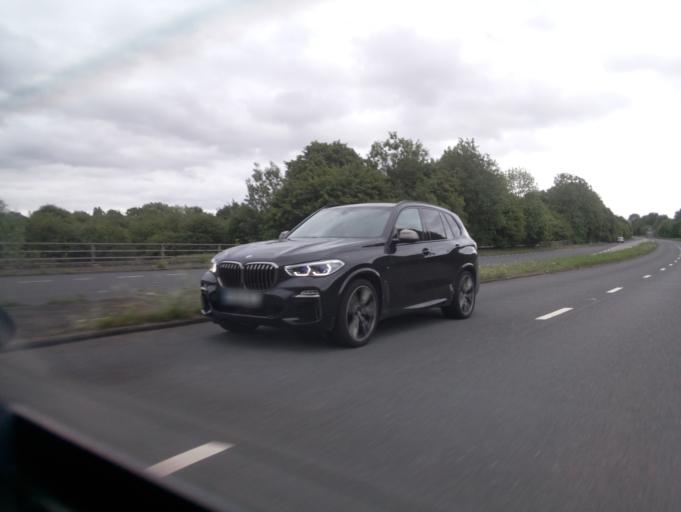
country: GB
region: England
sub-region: Worcestershire
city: Droitwich
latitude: 52.2599
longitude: -2.1769
